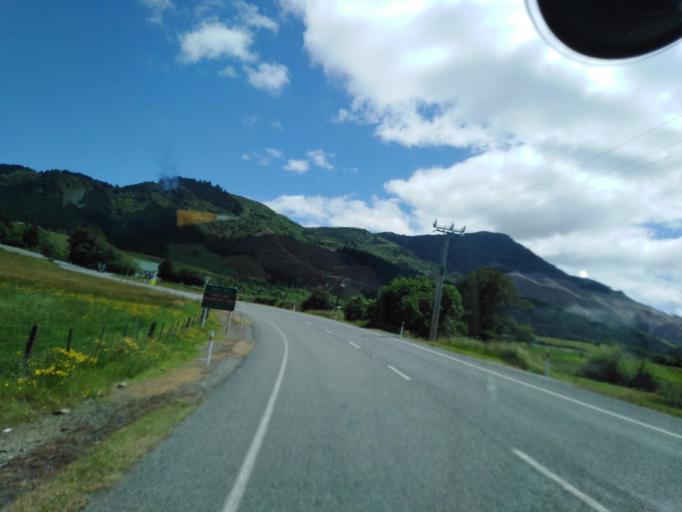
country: NZ
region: Nelson
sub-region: Nelson City
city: Nelson
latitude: -41.2126
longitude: 173.3959
